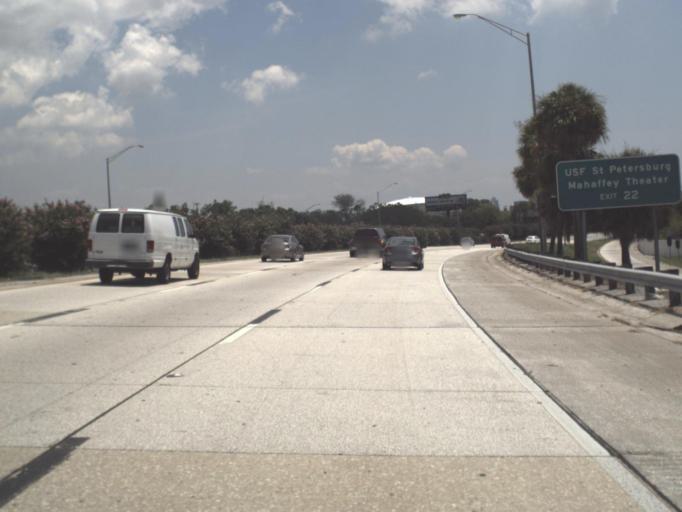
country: US
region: Florida
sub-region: Pinellas County
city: Saint Petersburg
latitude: 27.7608
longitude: -82.6707
